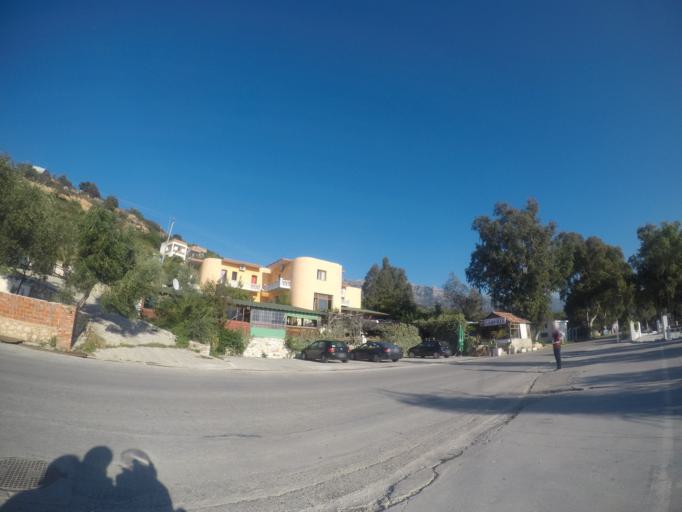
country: AL
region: Vlore
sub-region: Rrethi i Vlores
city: Orikum
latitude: 40.3613
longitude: 19.4804
